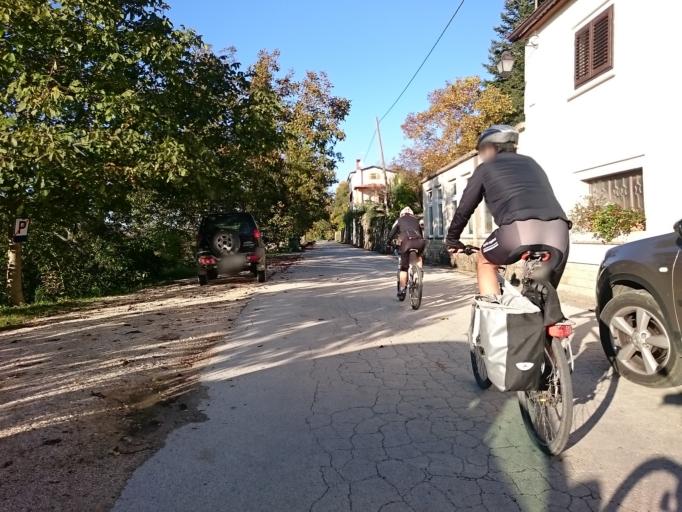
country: HR
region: Istarska
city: Buje
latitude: 45.3808
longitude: 13.7228
